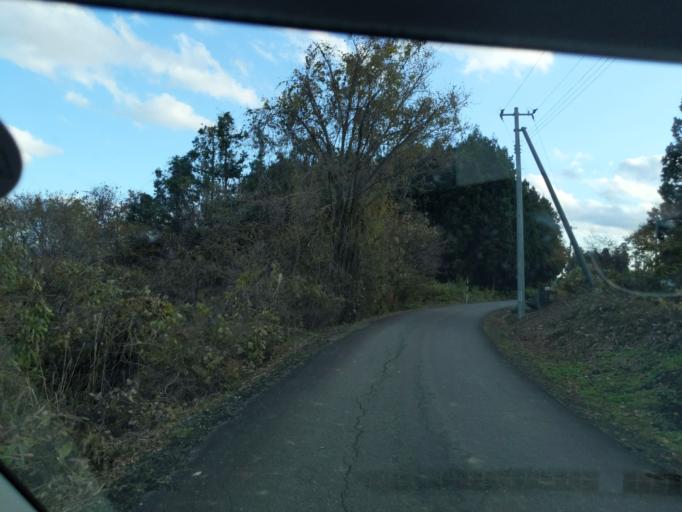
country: JP
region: Iwate
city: Mizusawa
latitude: 39.1089
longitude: 141.0394
